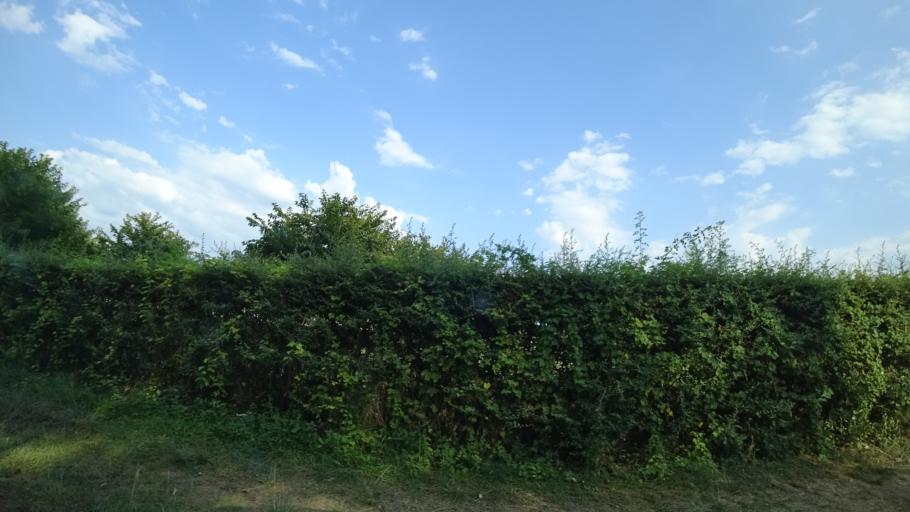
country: FR
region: Midi-Pyrenees
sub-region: Departement de l'Aveyron
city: Livinhac-le-Haut
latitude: 44.6092
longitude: 2.2342
